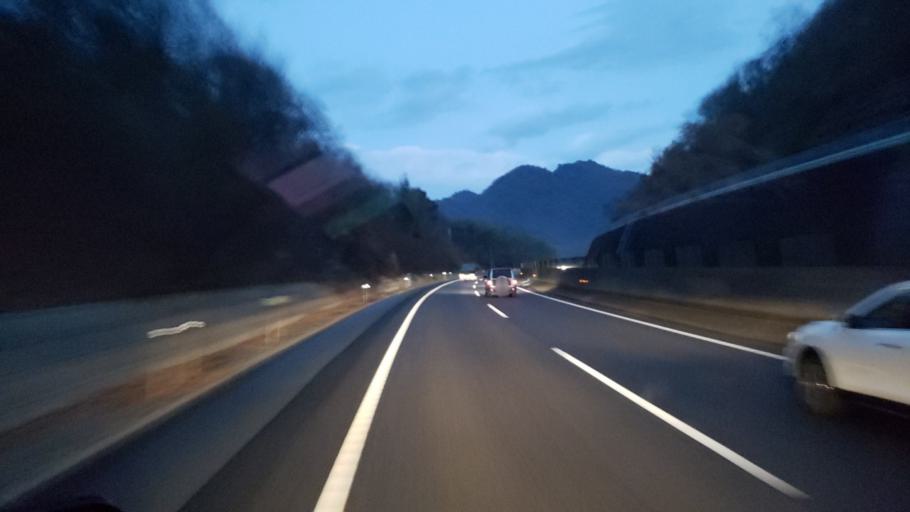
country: JP
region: Hyogo
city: Kakogawacho-honmachi
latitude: 34.8499
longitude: 134.8046
